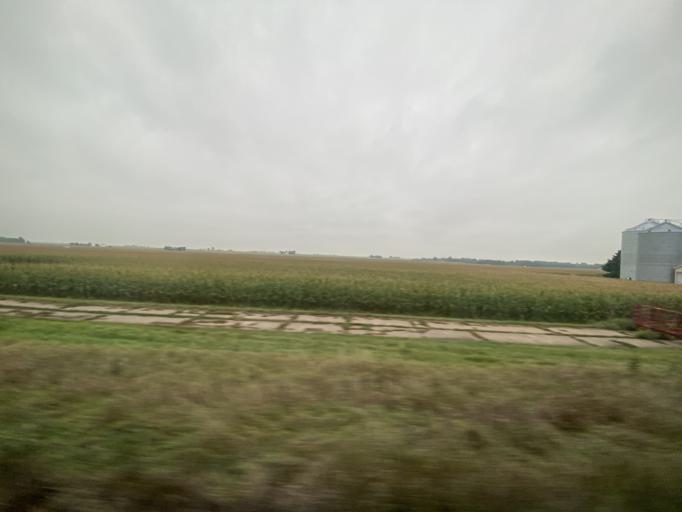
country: US
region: Illinois
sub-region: DeKalb County
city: Somonauk
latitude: 41.6226
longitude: -88.7476
